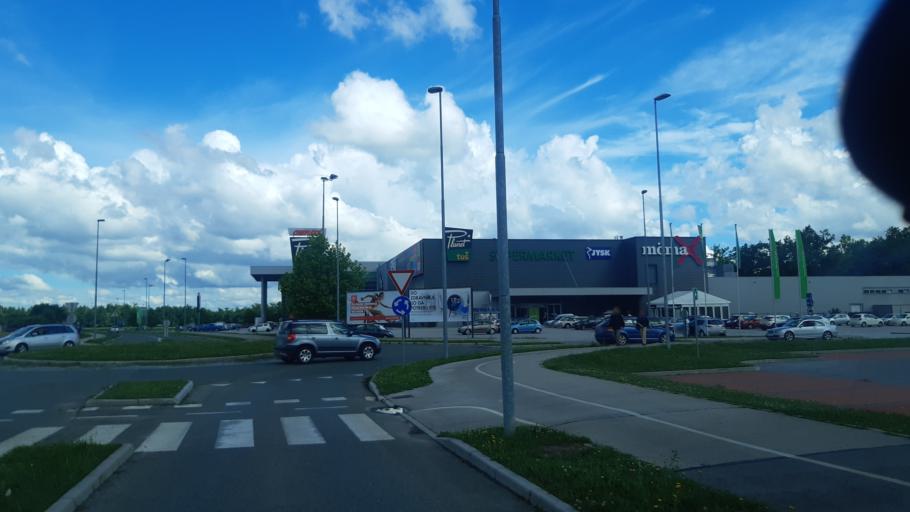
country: SI
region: Kranj
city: Kranj
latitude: 46.2378
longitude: 14.3717
